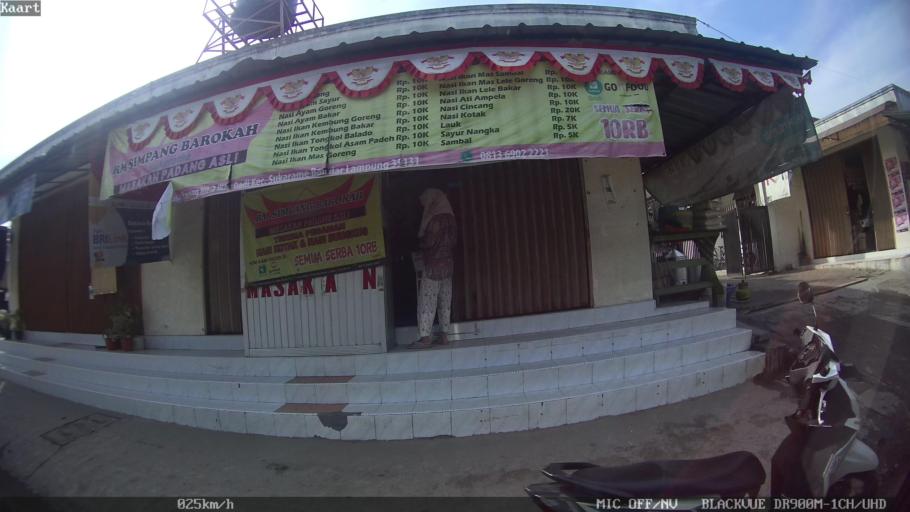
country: ID
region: Lampung
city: Kedaton
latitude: -5.3814
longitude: 105.2969
